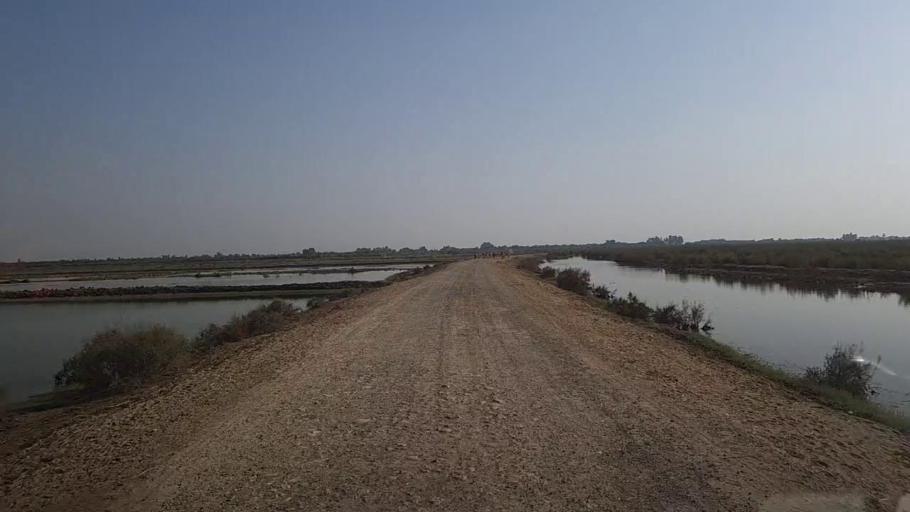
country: PK
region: Sindh
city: Kandhkot
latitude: 28.3642
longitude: 69.3298
